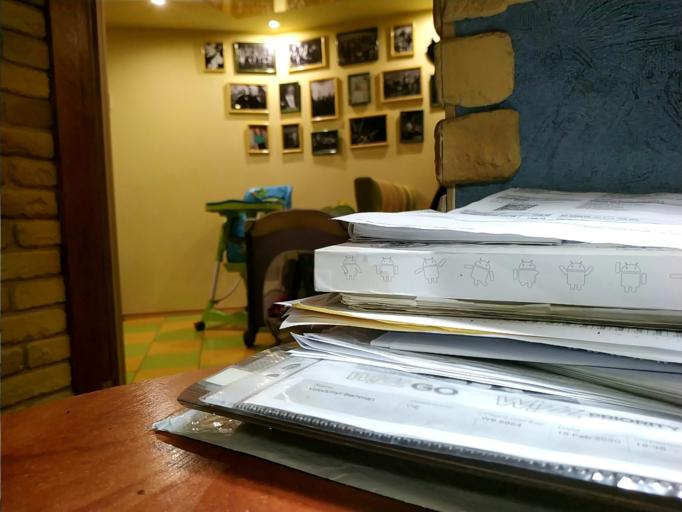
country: RU
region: Arkhangelskaya
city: Kargopol'
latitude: 61.4506
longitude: 39.3524
